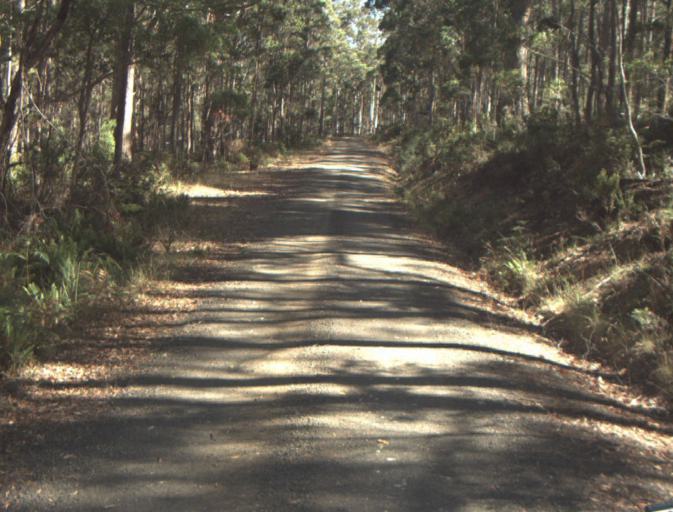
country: AU
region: Tasmania
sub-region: Launceston
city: Newstead
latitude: -41.3036
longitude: 147.3173
